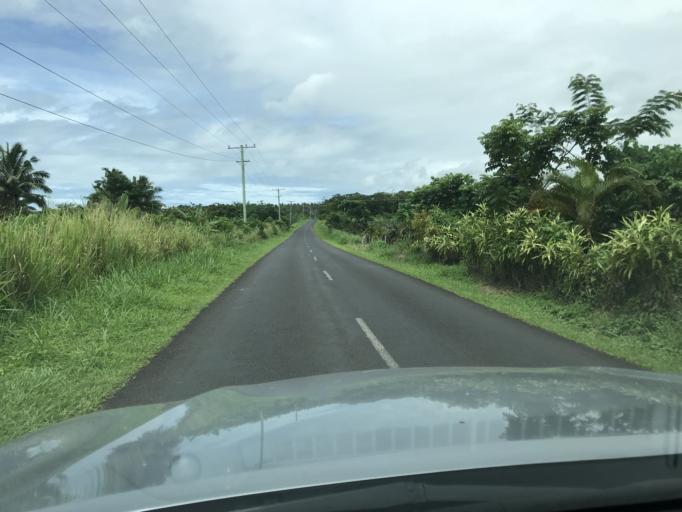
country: WS
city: Nofoali`i
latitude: -13.8744
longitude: -171.9282
